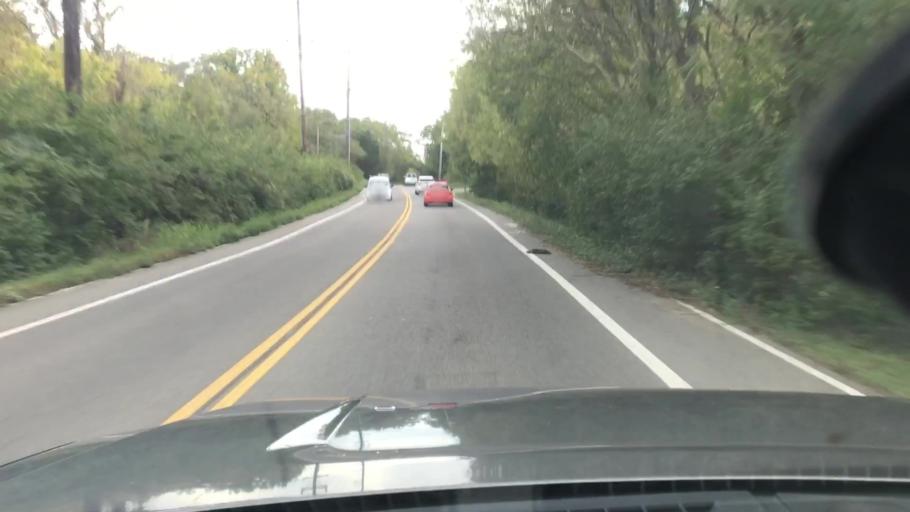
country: US
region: Tennessee
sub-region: Davidson County
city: Forest Hills
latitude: 36.0827
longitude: -86.8339
